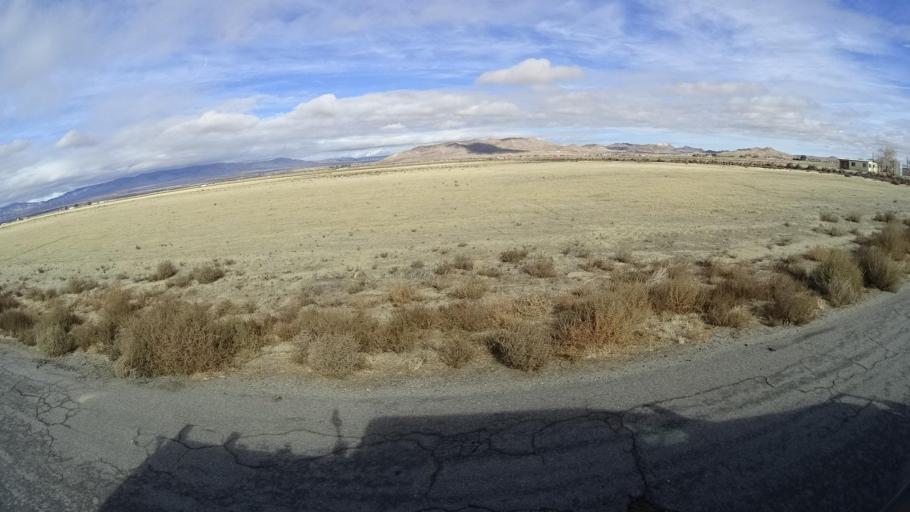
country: US
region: California
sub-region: Kern County
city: Rosamond
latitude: 34.8346
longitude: -118.2826
